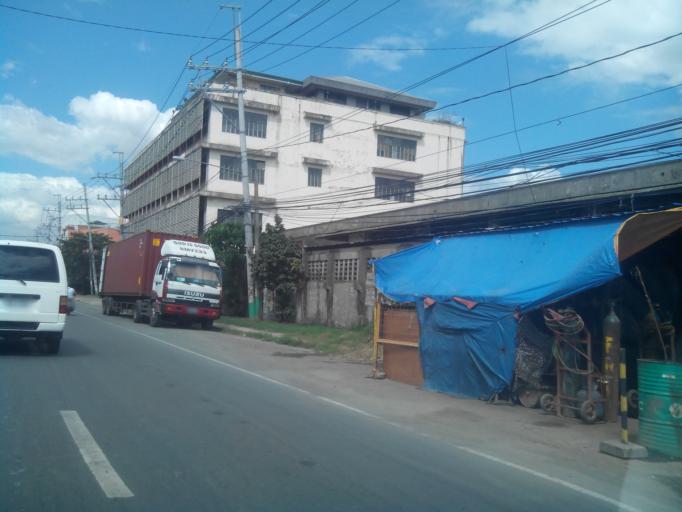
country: PH
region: Calabarzon
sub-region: Province of Rizal
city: Taytay
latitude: 14.5500
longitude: 121.1403
